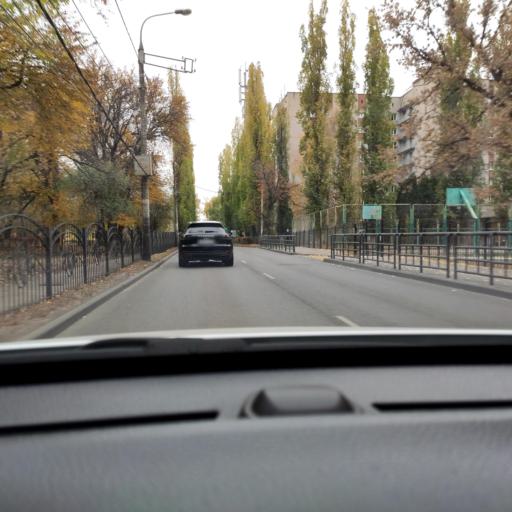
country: RU
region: Voronezj
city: Voronezh
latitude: 51.7138
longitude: 39.2282
